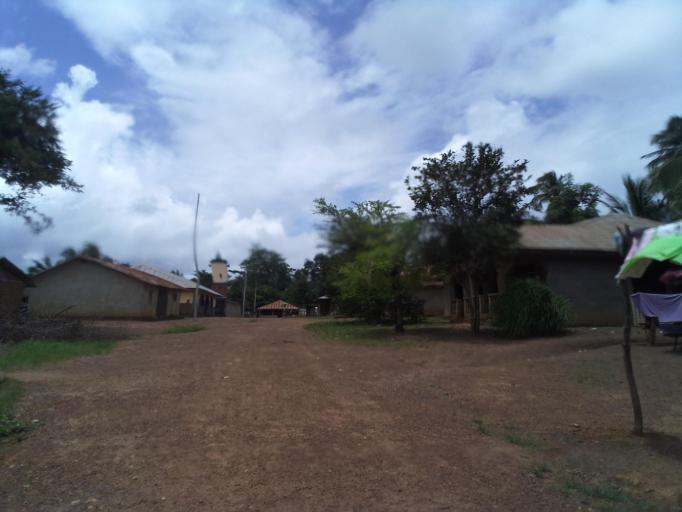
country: SL
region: Eastern Province
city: Kenema
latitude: 7.8140
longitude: -11.1781
